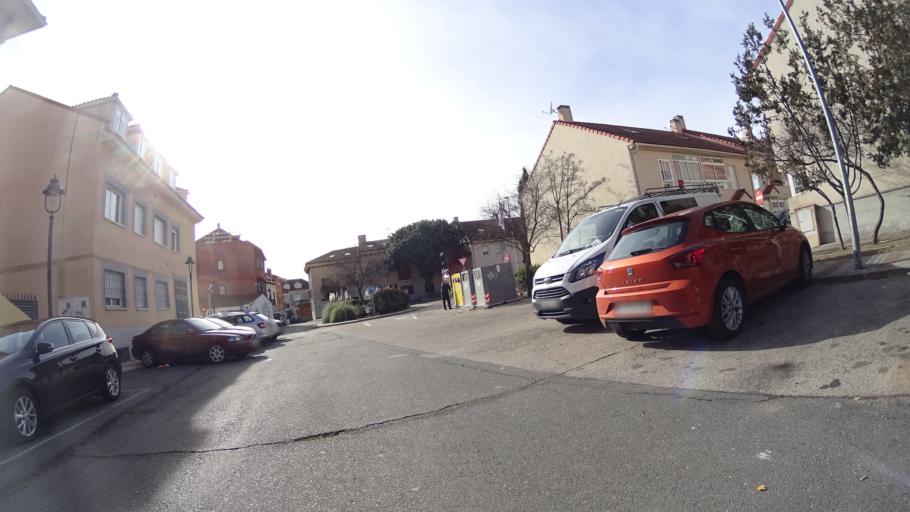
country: ES
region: Madrid
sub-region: Provincia de Madrid
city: Moralzarzal
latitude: 40.6802
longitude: -3.9736
